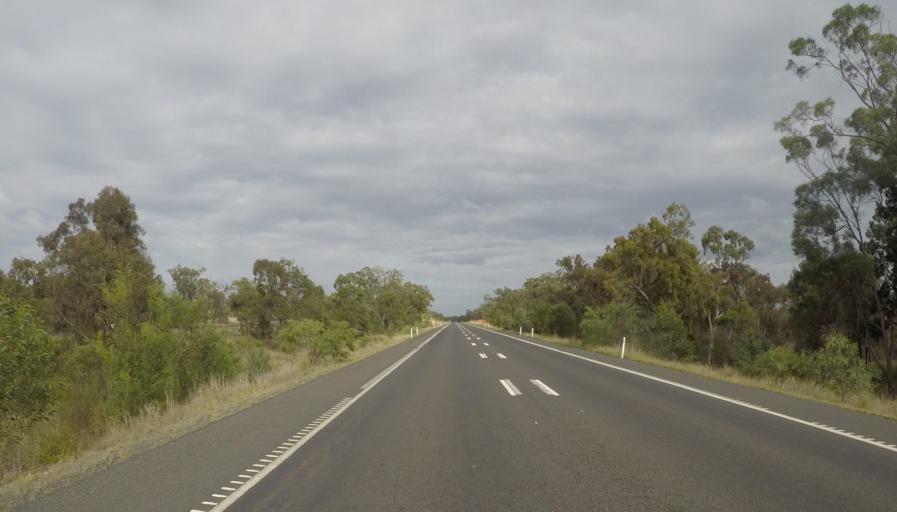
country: AU
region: Queensland
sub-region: Western Downs
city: Westcourt
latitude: -26.6607
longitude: 150.2430
